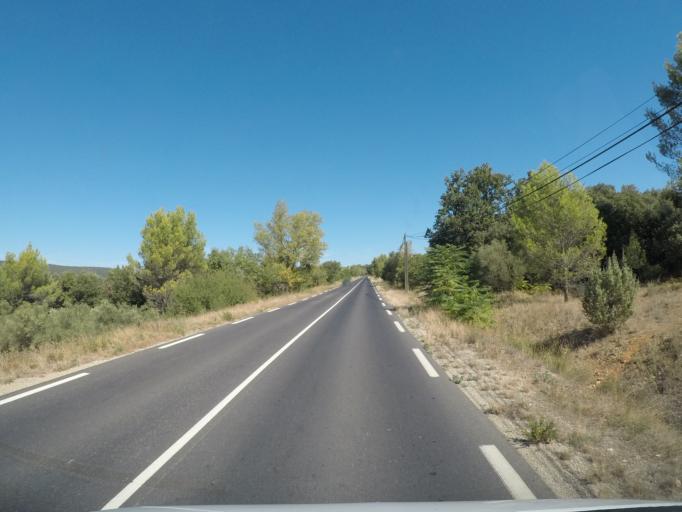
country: FR
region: Languedoc-Roussillon
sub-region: Departement de l'Herault
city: Aniane
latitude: 43.6991
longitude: 3.5916
